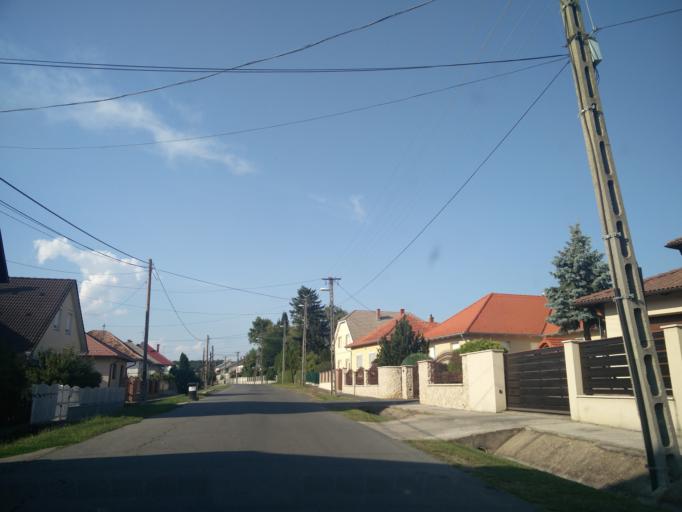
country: HU
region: Zala
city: Zalaegerszeg
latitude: 46.8626
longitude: 16.8021
